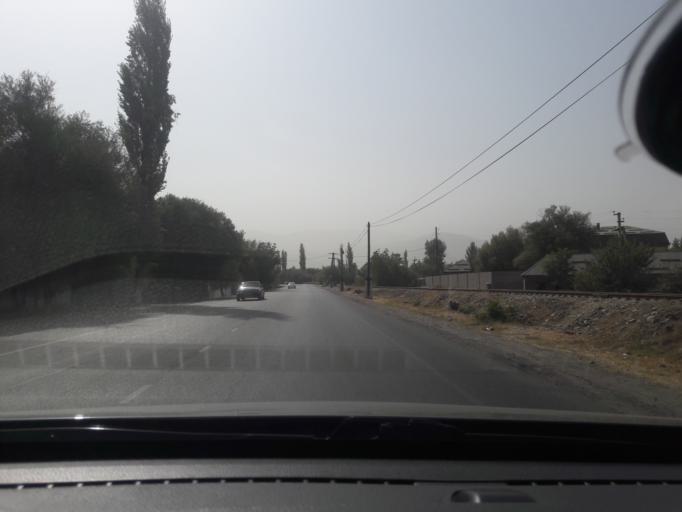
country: TJ
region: Republican Subordination
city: Vahdat
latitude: 38.5222
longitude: 69.0283
